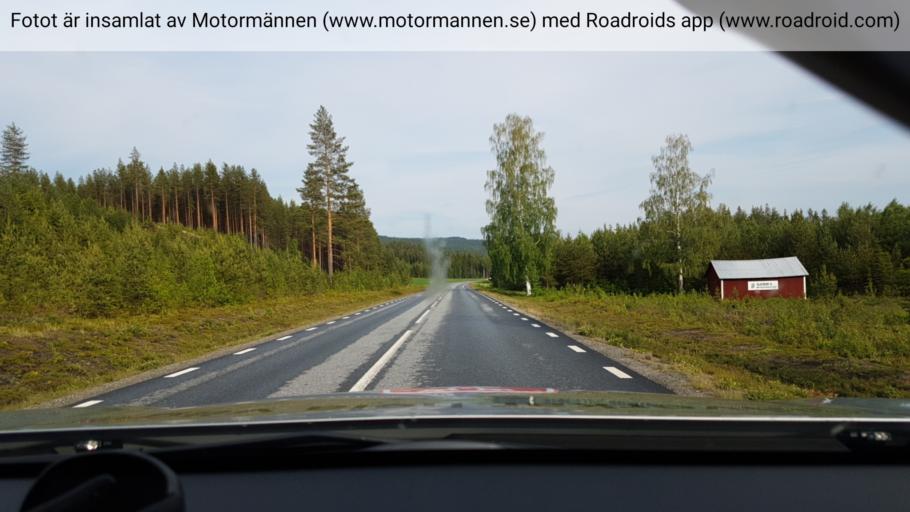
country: SE
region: Vaesterbotten
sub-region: Bjurholms Kommun
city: Bjurholm
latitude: 64.2816
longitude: 19.2354
